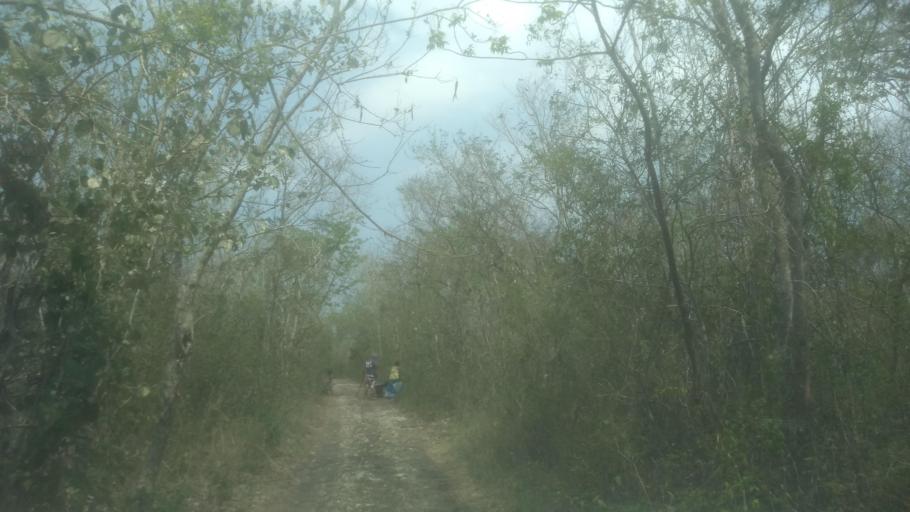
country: MX
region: Veracruz
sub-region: Emiliano Zapata
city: Plan del Rio
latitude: 19.3888
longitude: -96.6302
